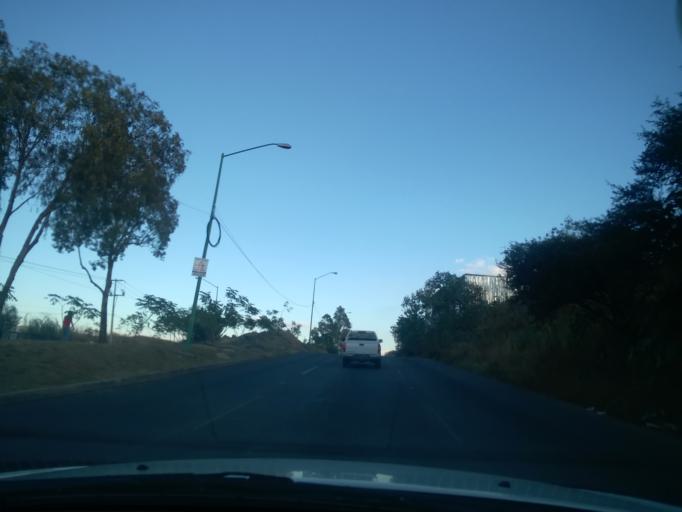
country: MX
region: Guanajuato
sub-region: Leon
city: Ejido la Joya
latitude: 21.1360
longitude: -101.7198
